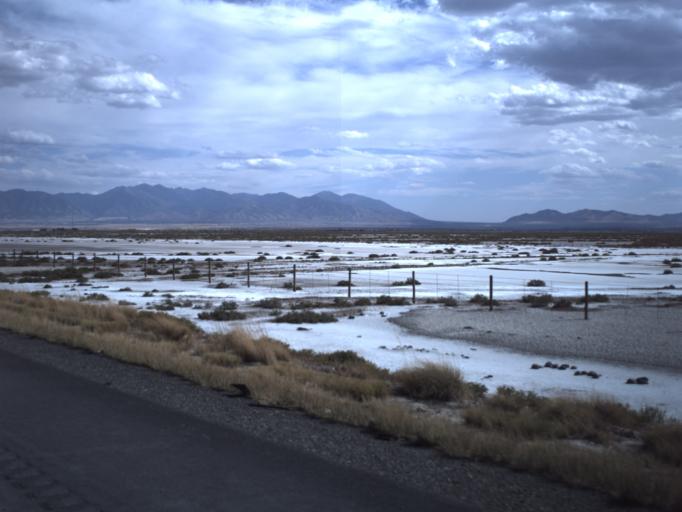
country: US
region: Utah
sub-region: Tooele County
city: Grantsville
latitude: 40.6995
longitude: -112.4861
